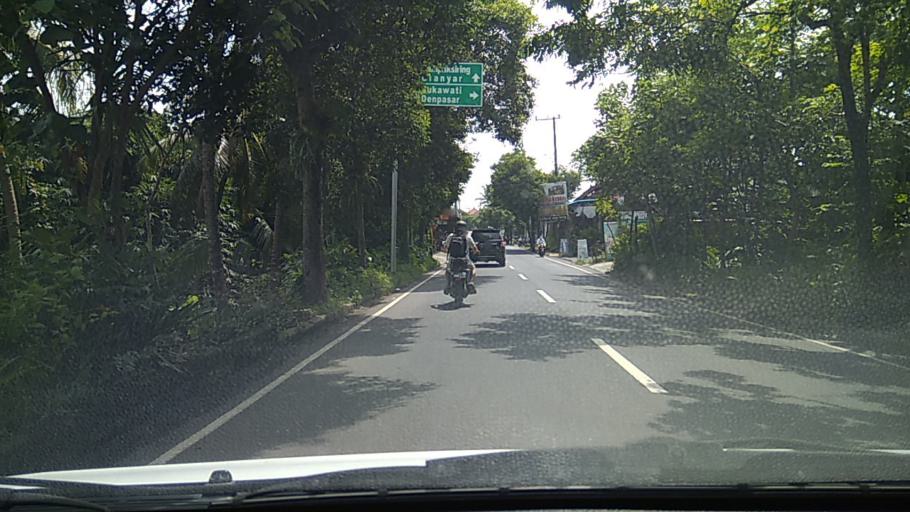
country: ID
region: Bali
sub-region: Kabupaten Gianyar
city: Ubud
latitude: -8.5239
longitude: 115.2699
